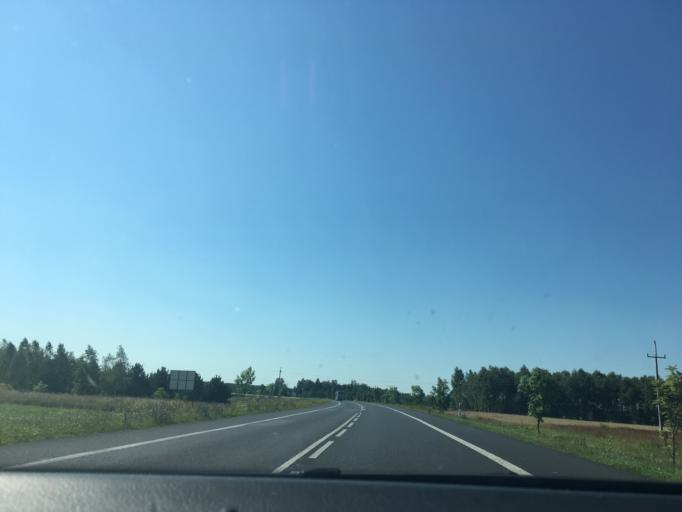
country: PL
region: Lublin Voivodeship
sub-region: Powiat lubartowski
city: Lubartow
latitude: 51.4593
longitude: 22.5755
